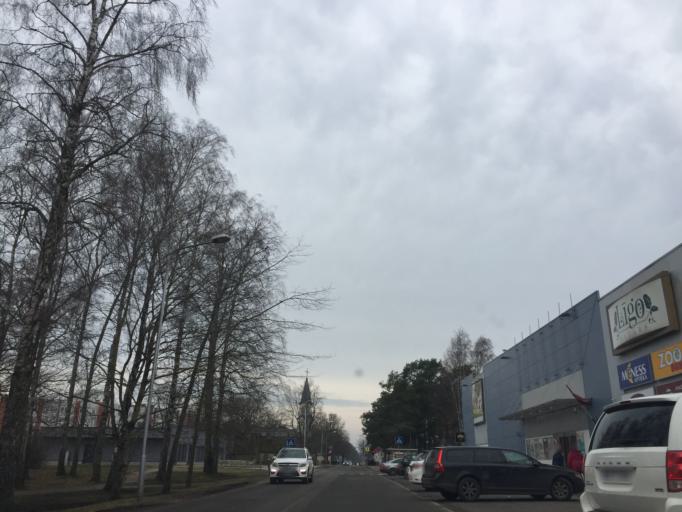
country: LV
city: Tireli
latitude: 56.9596
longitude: 23.6116
